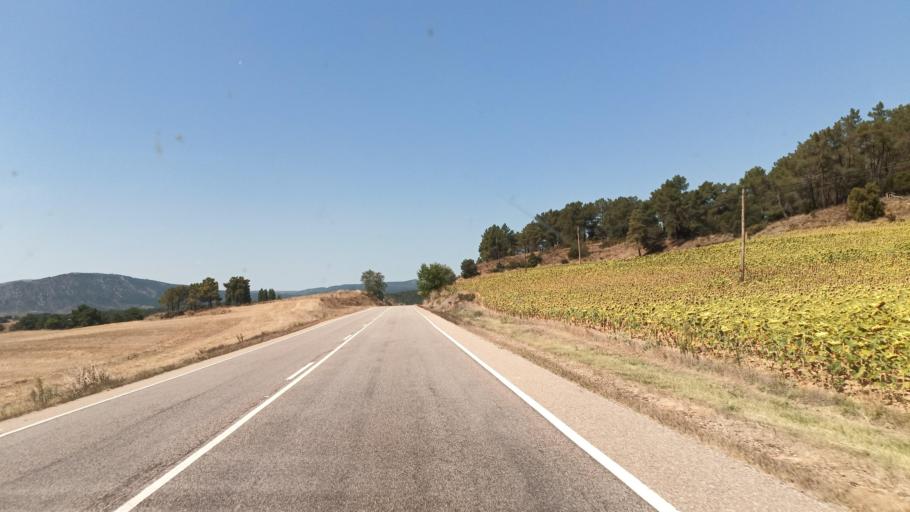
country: ES
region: Castille and Leon
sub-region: Provincia de Burgos
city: Salas de Bureba
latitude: 42.6727
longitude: -3.4173
